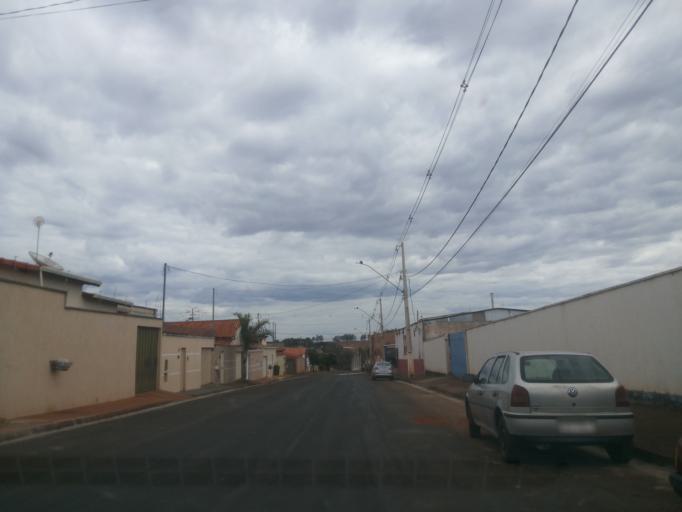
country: BR
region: Minas Gerais
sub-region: Centralina
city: Centralina
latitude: -18.7284
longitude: -49.1995
